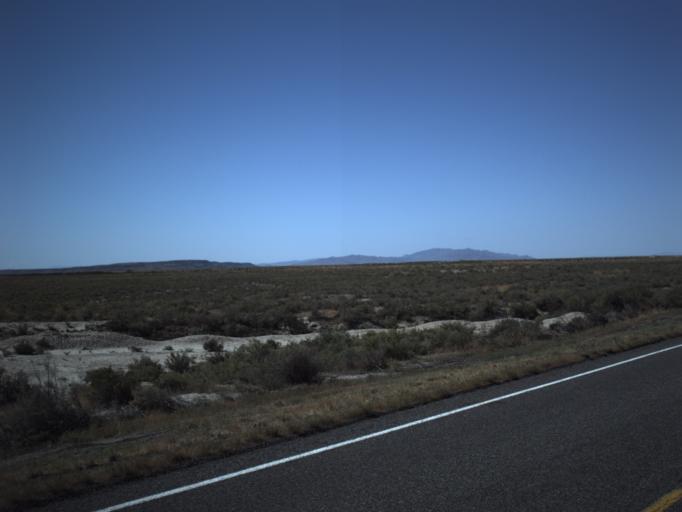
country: US
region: Utah
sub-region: Millard County
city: Delta
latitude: 39.3241
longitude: -112.7337
